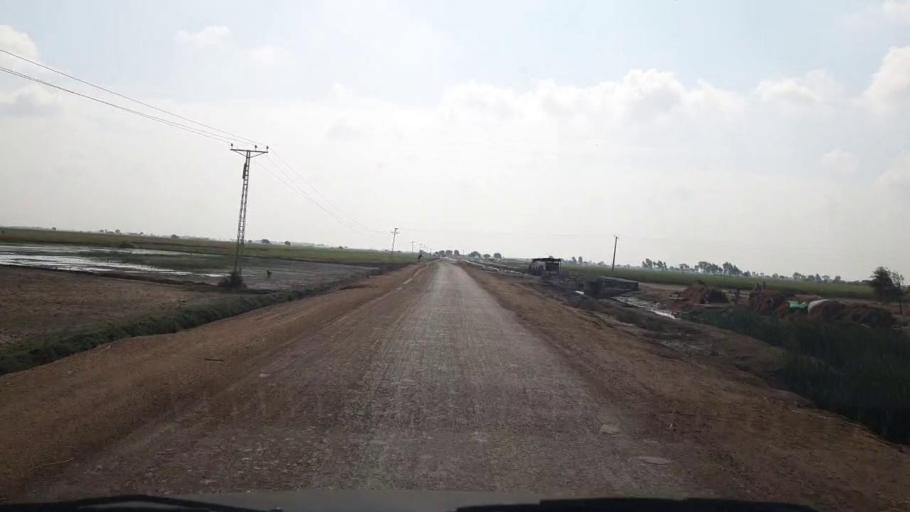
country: PK
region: Sindh
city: Kario
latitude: 24.6242
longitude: 68.5546
